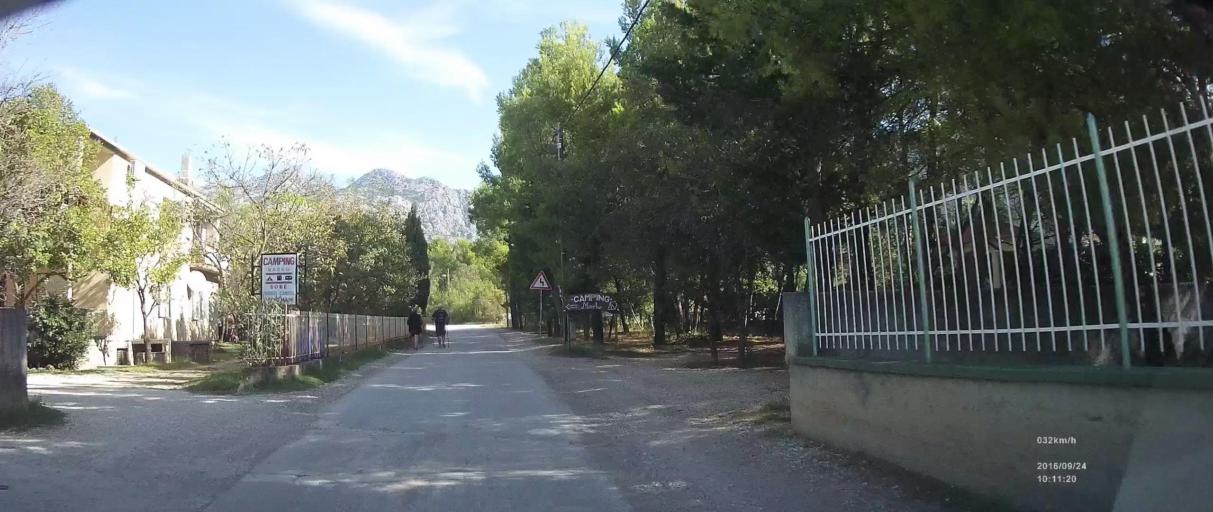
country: HR
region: Zadarska
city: Starigrad
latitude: 44.2863
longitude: 15.4525
